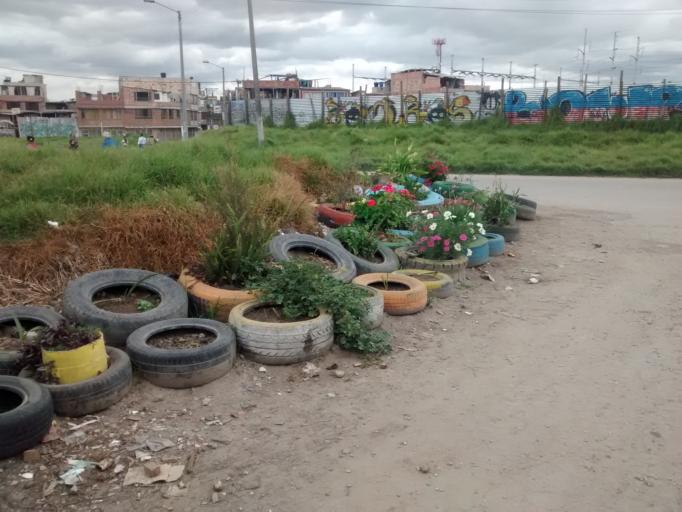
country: CO
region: Cundinamarca
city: Cota
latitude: 4.7290
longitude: -74.1031
